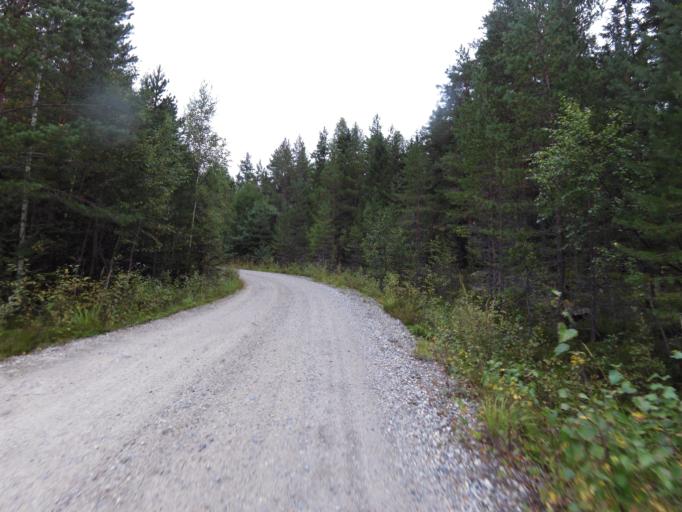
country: SE
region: Gaevleborg
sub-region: Gavle Kommun
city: Valbo
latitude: 60.7333
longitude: 17.0282
